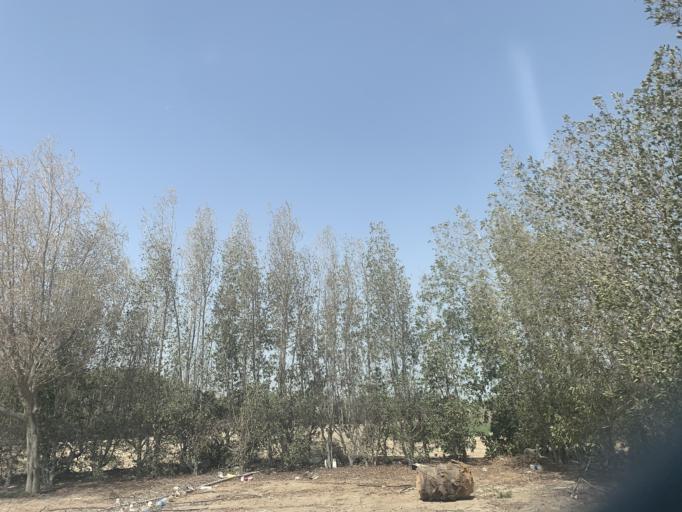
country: BH
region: Manama
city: Jidd Hafs
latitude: 26.2003
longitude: 50.5462
